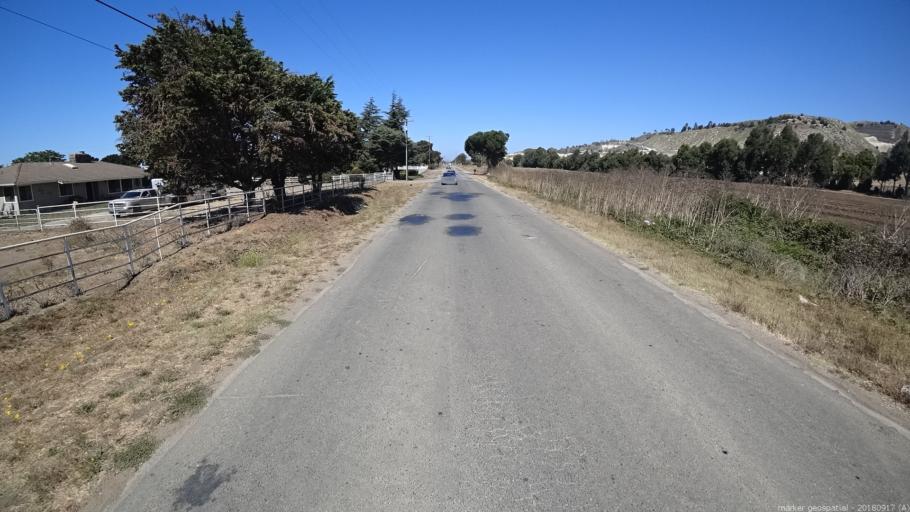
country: US
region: California
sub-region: Monterey County
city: Prunedale
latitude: 36.7371
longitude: -121.5998
